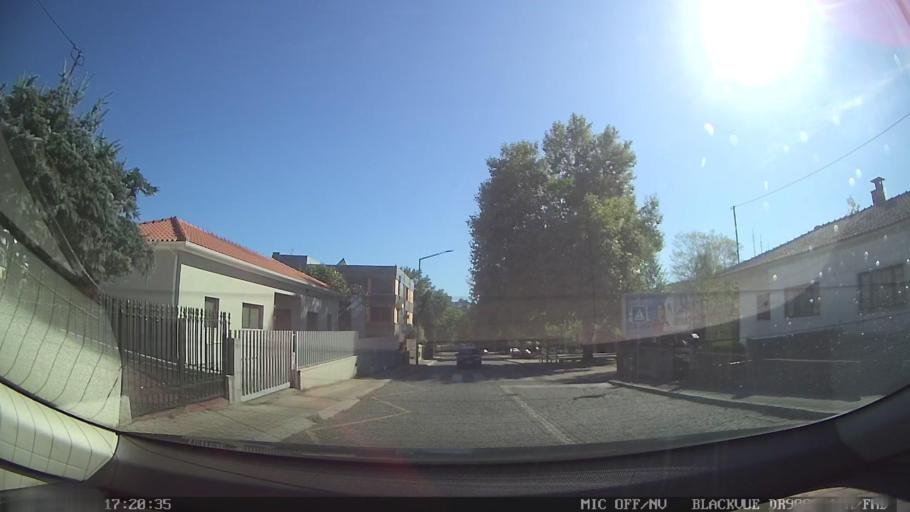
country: PT
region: Porto
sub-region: Santo Tirso
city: Santo Tirso
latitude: 41.3421
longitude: -8.4826
